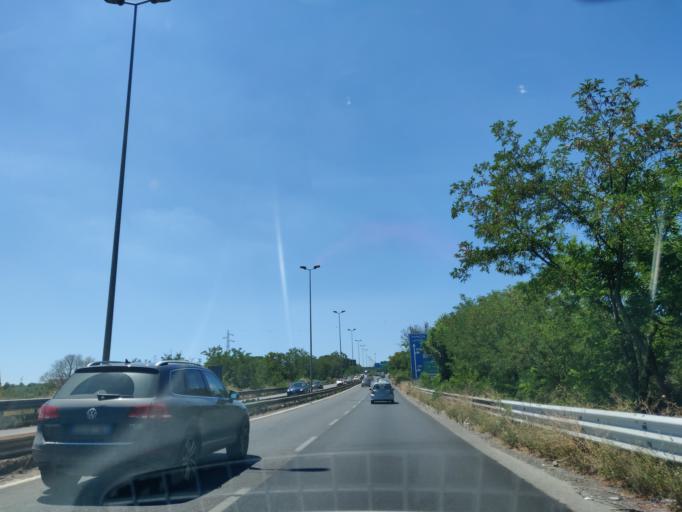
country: IT
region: Latium
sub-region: Citta metropolitana di Roma Capitale
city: Selcetta
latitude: 41.8086
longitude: 12.4572
